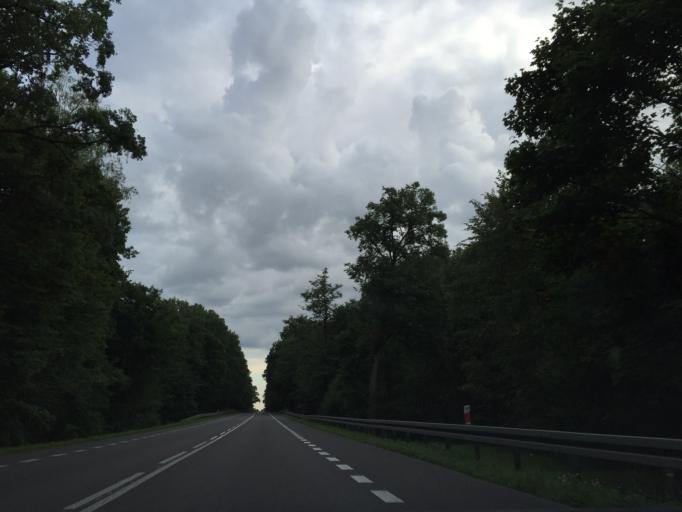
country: PL
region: Lublin Voivodeship
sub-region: Powiat radzynski
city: Borki
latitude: 51.7334
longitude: 22.5438
